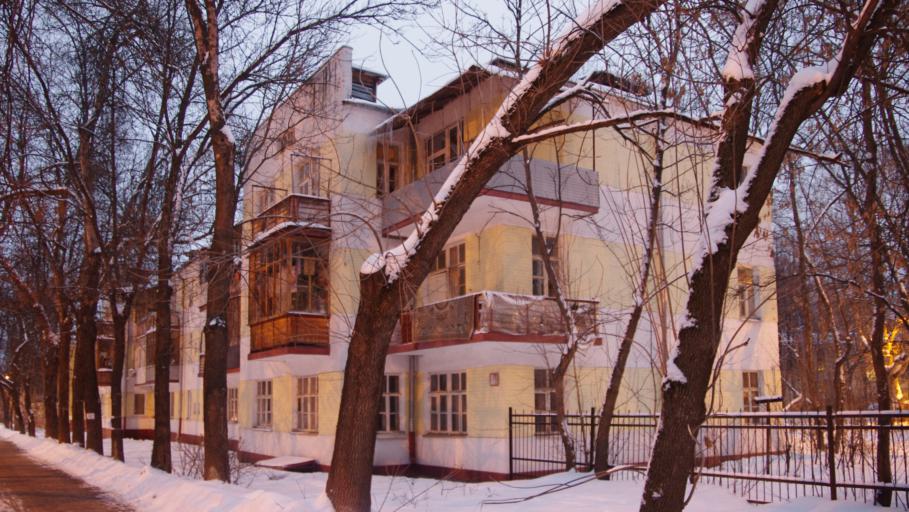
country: RU
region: Moskovskaya
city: Korolev
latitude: 55.9224
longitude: 37.8088
